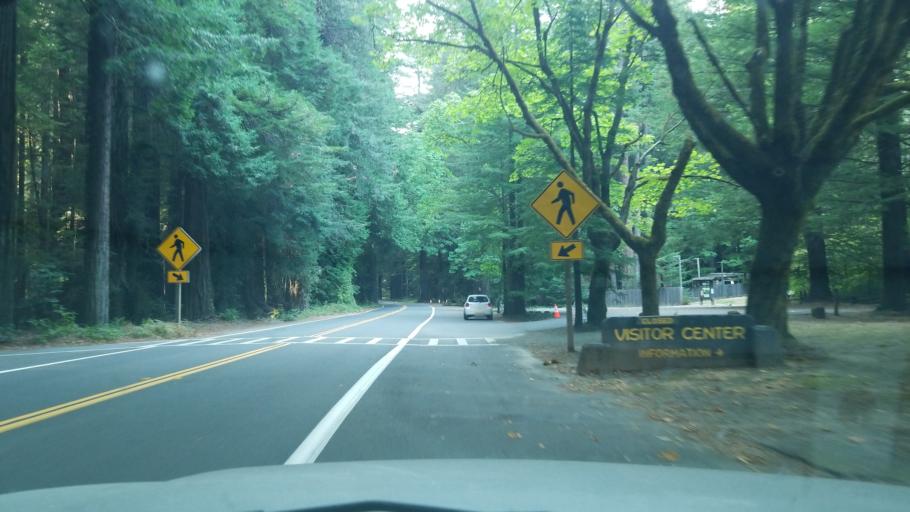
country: US
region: California
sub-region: Humboldt County
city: Redway
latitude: 40.3076
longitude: -123.9082
